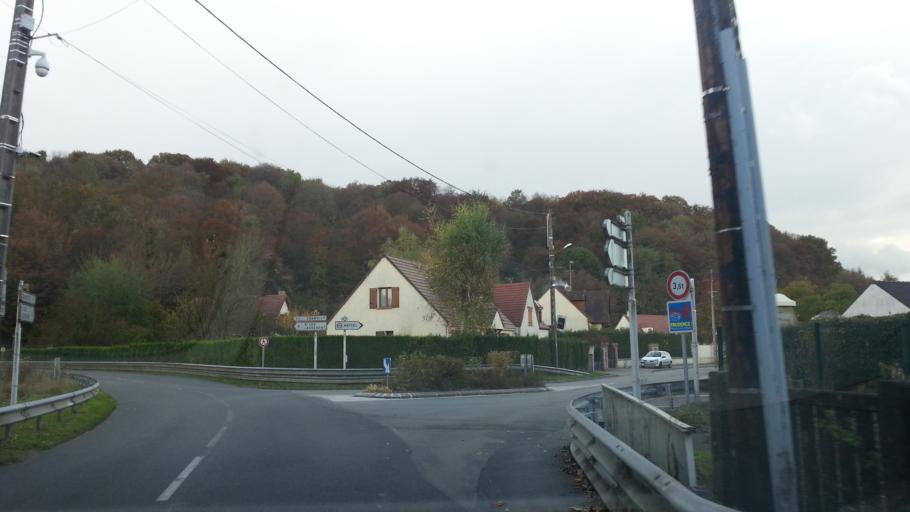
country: FR
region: Picardie
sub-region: Departement de l'Oise
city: Cires-les-Mello
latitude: 49.2617
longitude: 2.3781
